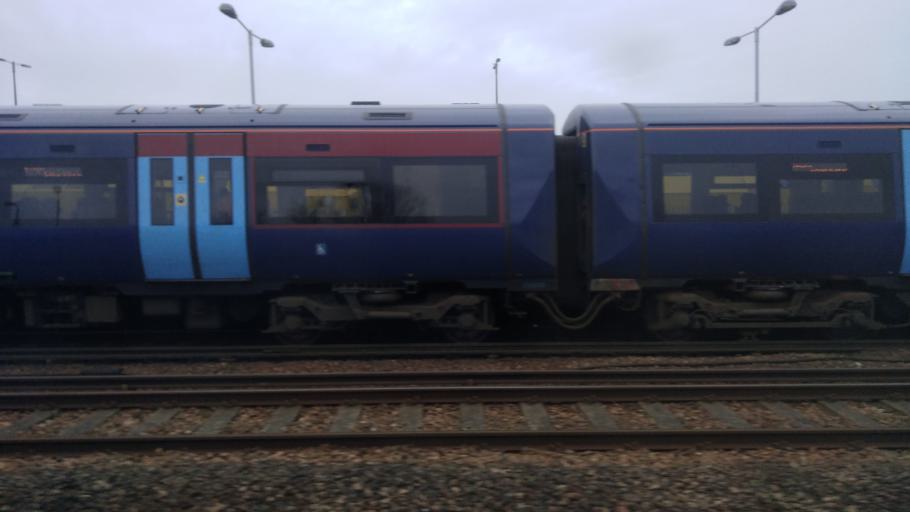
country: GB
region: England
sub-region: Kent
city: Paddock Wood
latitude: 51.1823
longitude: 0.3906
